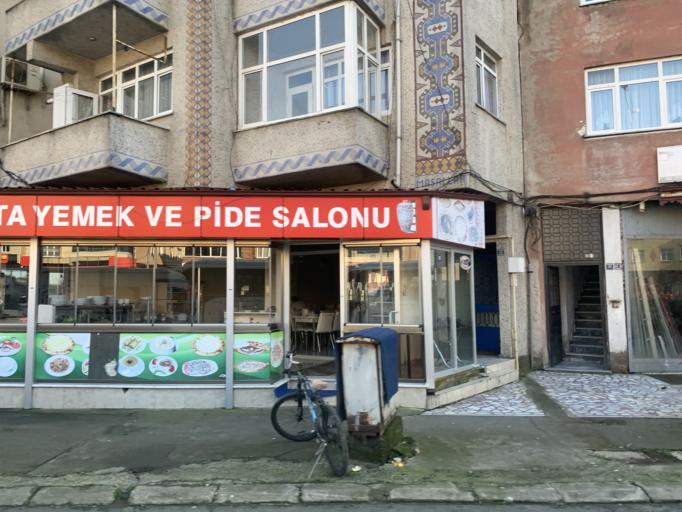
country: TR
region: Trabzon
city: Of
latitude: 40.9428
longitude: 40.2645
